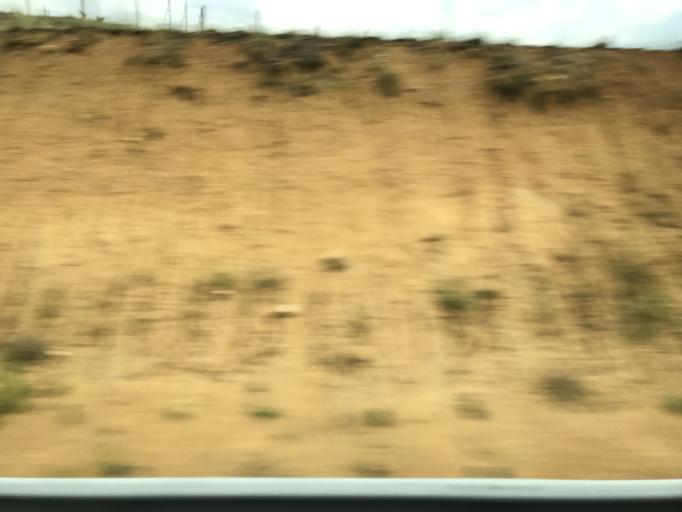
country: ES
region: Castille and Leon
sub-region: Provincia de Segovia
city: Cerezo de Abajo
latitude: 41.2437
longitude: -3.5922
